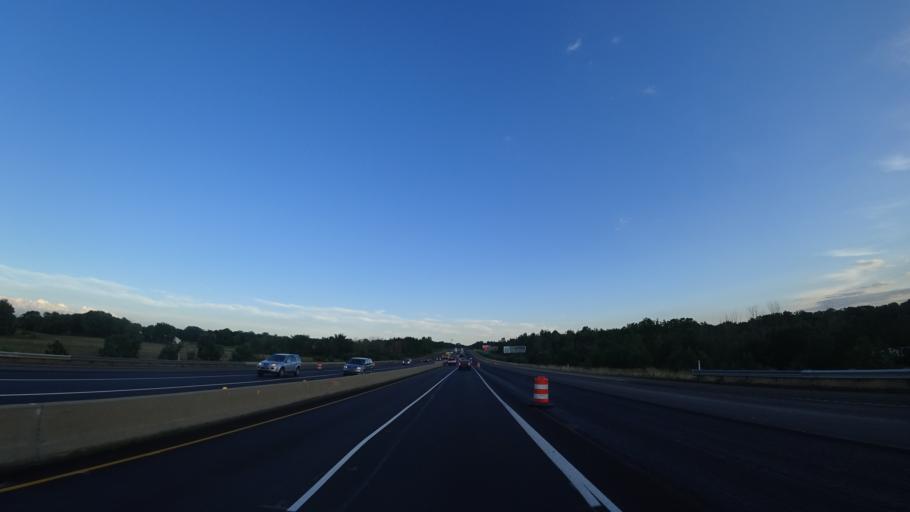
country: US
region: Indiana
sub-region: LaPorte County
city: Long Beach
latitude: 41.7166
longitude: -86.8058
